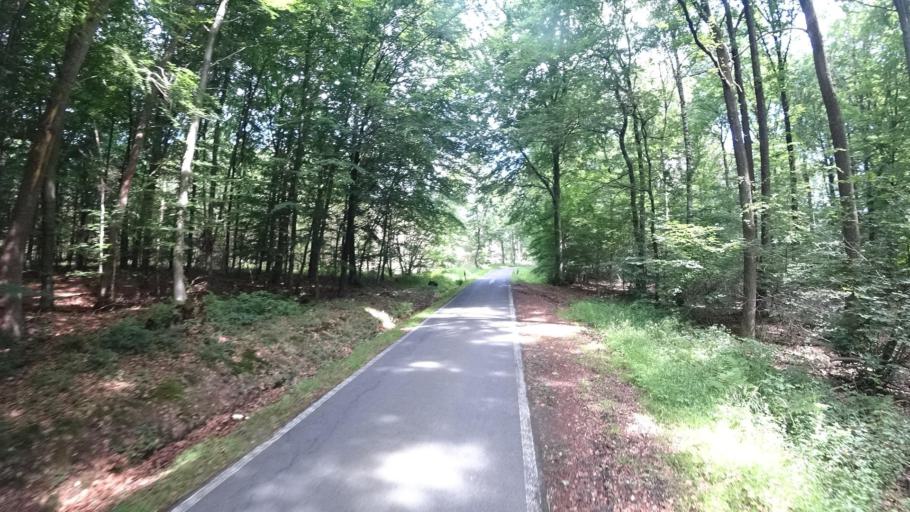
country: DE
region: Rheinland-Pfalz
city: Ratzert
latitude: 50.6577
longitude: 7.6233
